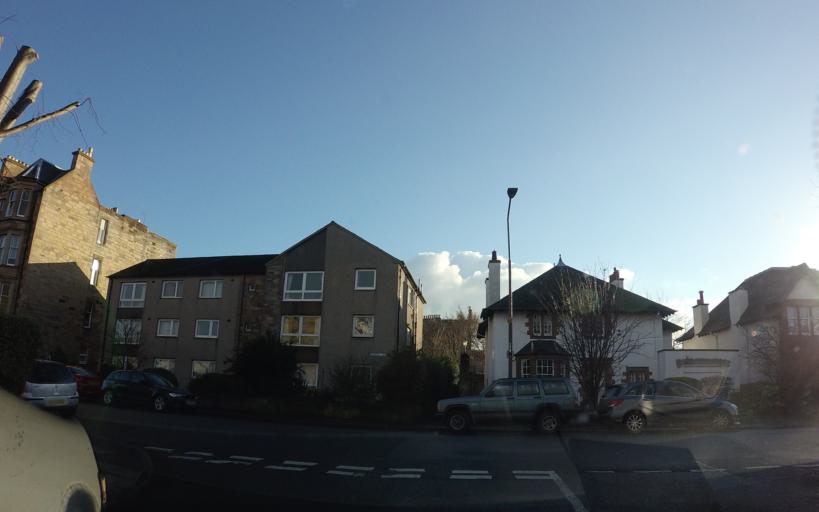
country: GB
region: Scotland
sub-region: Edinburgh
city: Edinburgh
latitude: 55.9746
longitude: -3.2113
